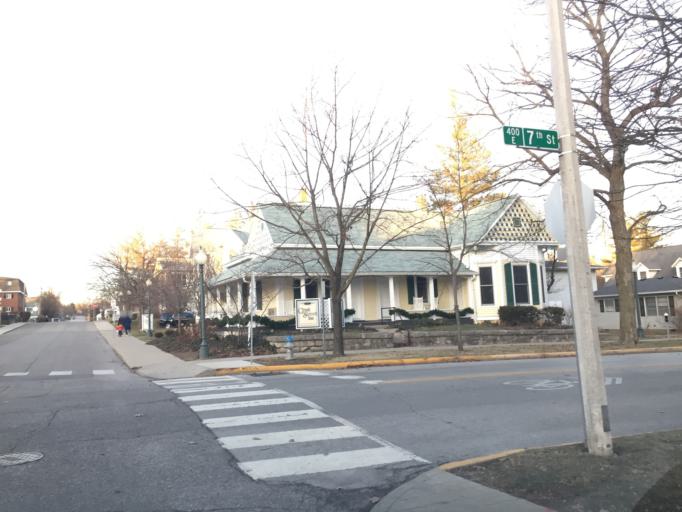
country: US
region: Indiana
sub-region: Monroe County
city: Bloomington
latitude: 39.1685
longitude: -86.5298
